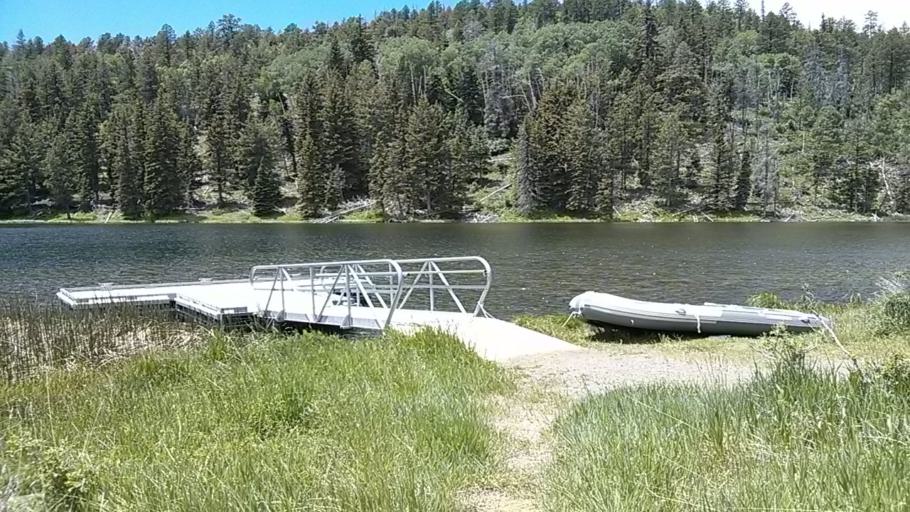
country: US
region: Utah
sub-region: Wayne County
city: Loa
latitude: 37.9378
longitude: -111.6955
